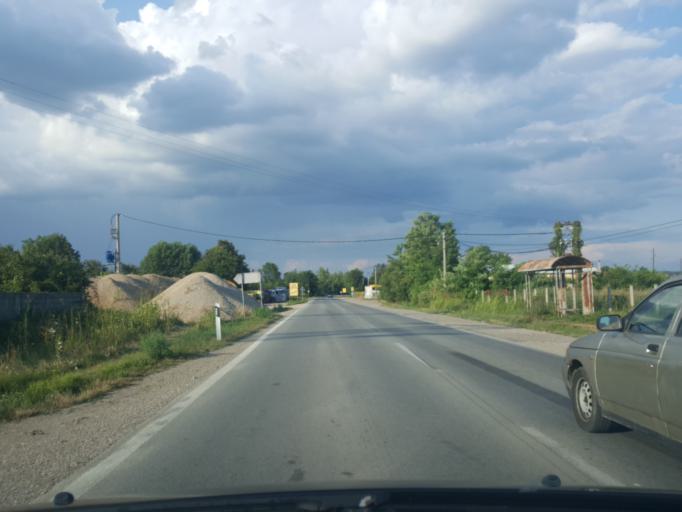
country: RS
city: Lesnica
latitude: 44.6409
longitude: 19.2806
